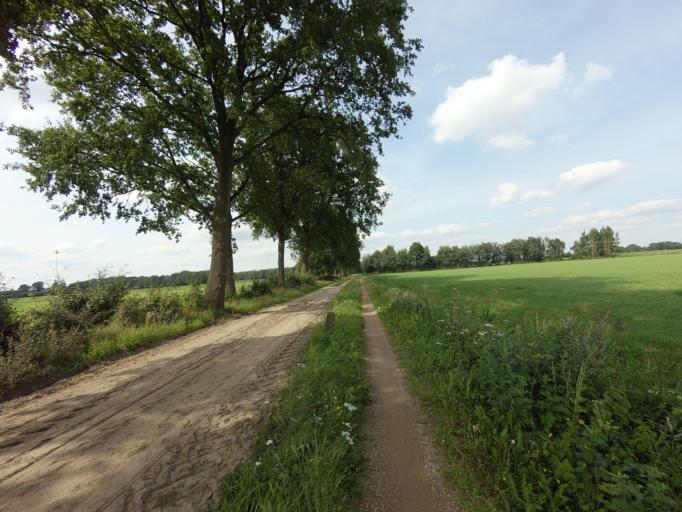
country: DE
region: Lower Saxony
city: Lage
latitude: 52.4277
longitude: 6.9497
